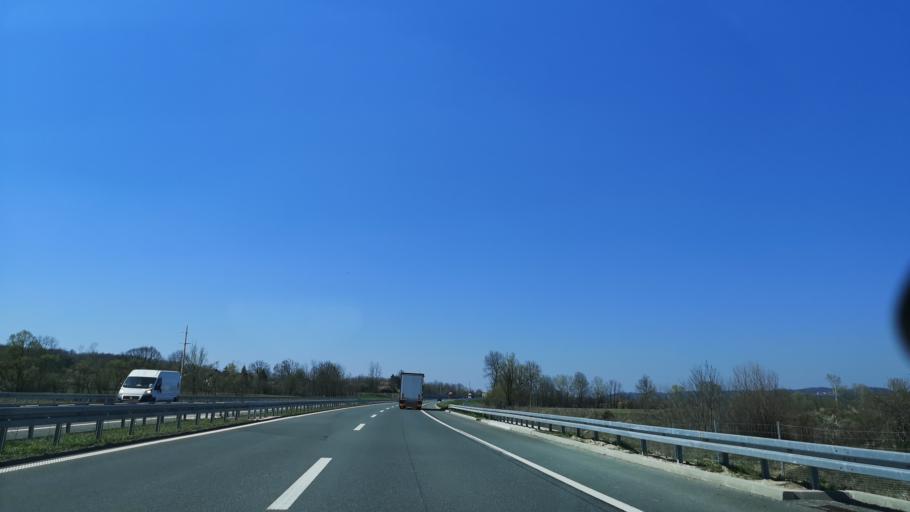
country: RS
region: Central Serbia
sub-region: Kolubarski Okrug
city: Ljig
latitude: 44.2908
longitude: 20.2408
